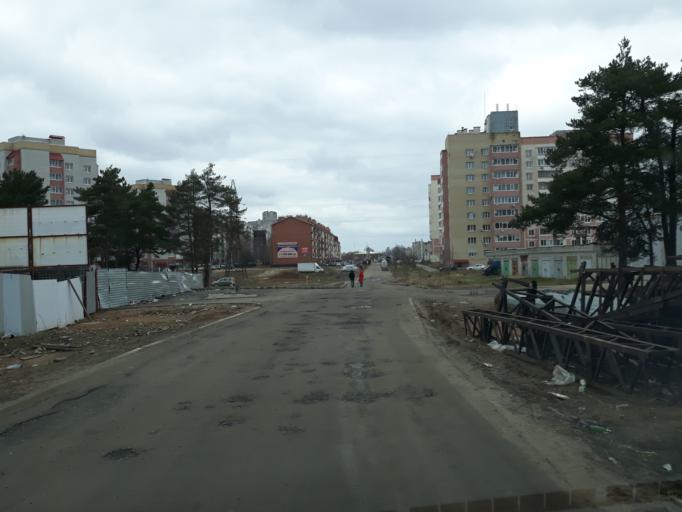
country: RU
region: Jaroslavl
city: Yaroslavl
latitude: 57.6482
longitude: 39.9700
